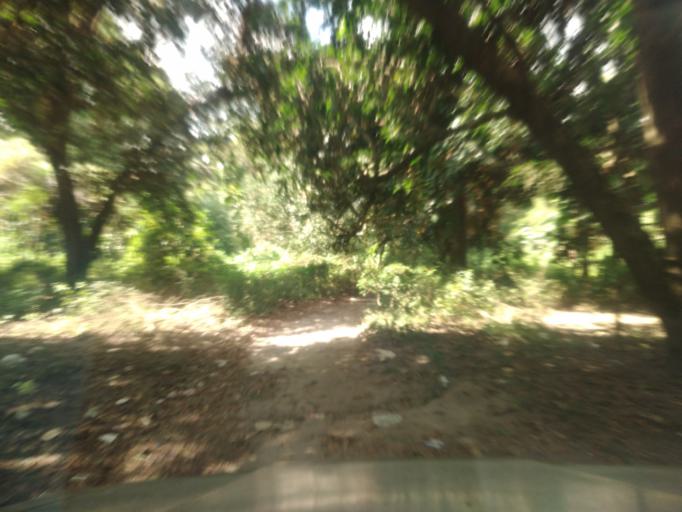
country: PH
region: Central Luzon
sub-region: Province of Pampanga
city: Balas
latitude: 15.0480
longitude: 120.5785
